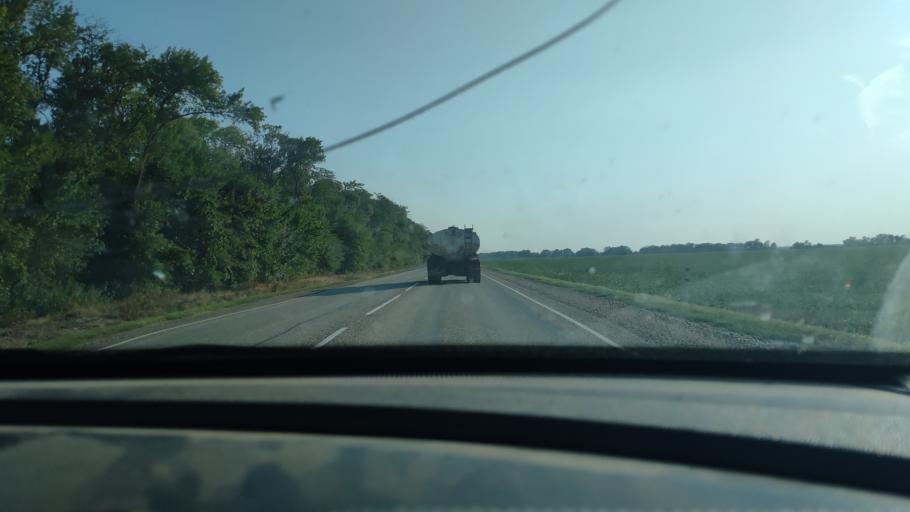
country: RU
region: Krasnodarskiy
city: Starominskaya
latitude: 46.4620
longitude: 39.0379
